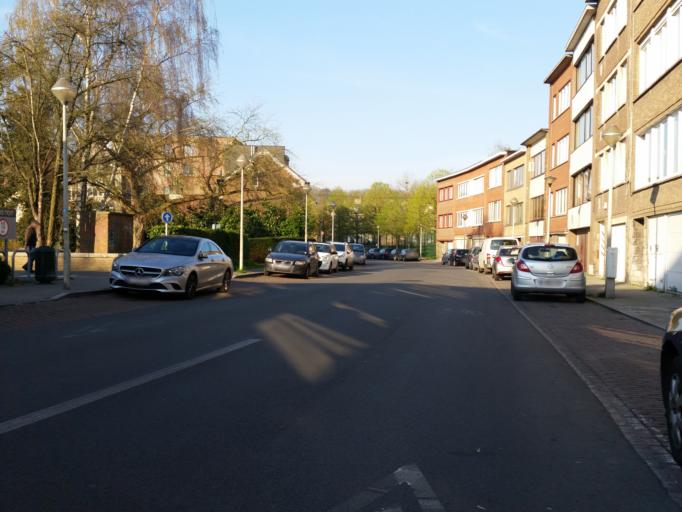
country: BE
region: Flanders
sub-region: Provincie Vlaams-Brabant
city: Grimbergen
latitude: 50.8909
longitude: 4.3792
